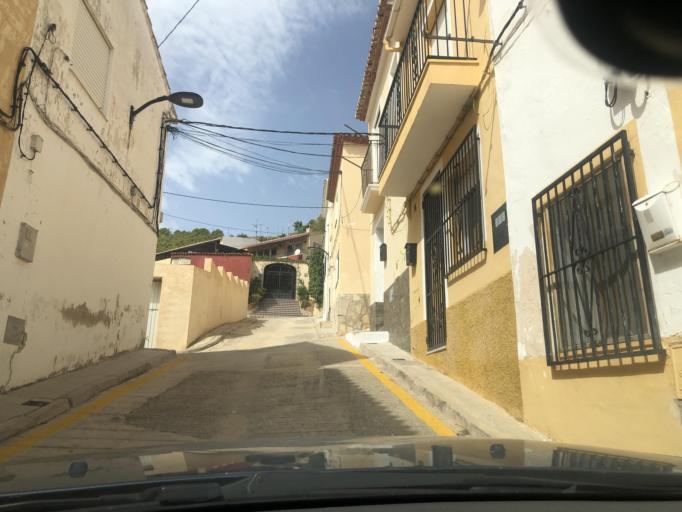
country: ES
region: Valencia
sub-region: Provincia de Alicante
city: Callosa d'En Sarria
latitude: 38.6540
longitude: -0.1219
